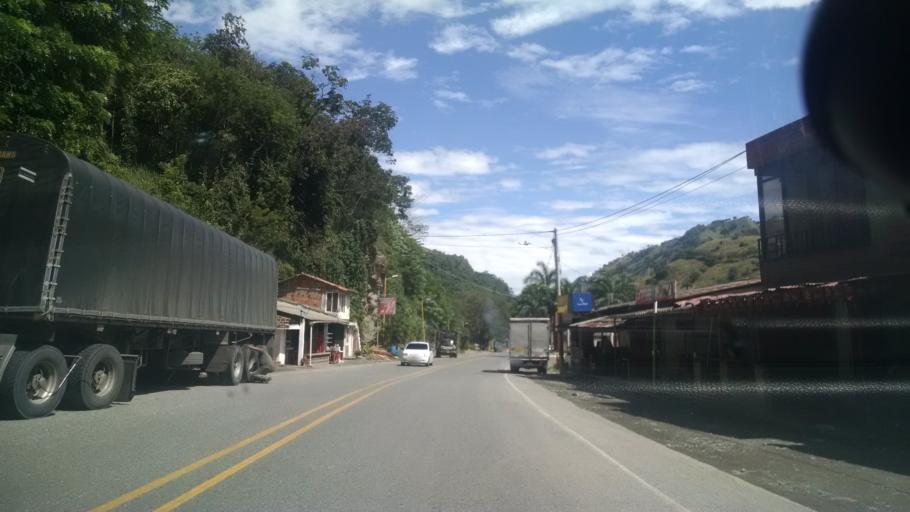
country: CO
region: Caldas
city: Supia
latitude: 5.3892
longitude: -75.6006
